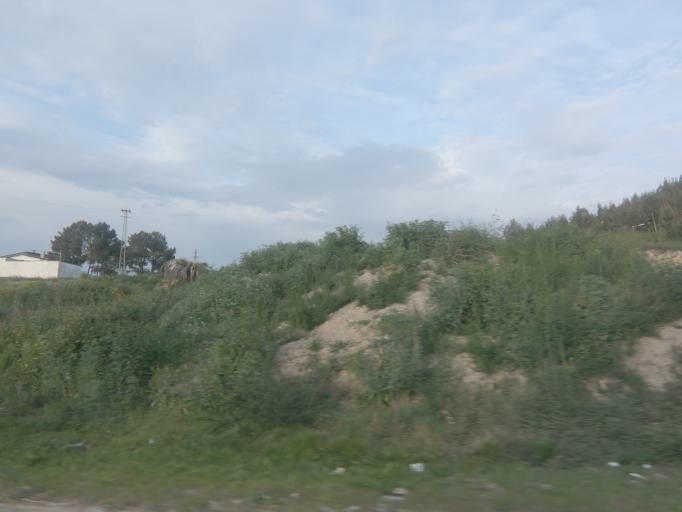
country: PT
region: Porto
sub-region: Gondomar
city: Baguim do Monte
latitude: 41.2013
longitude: -8.5265
